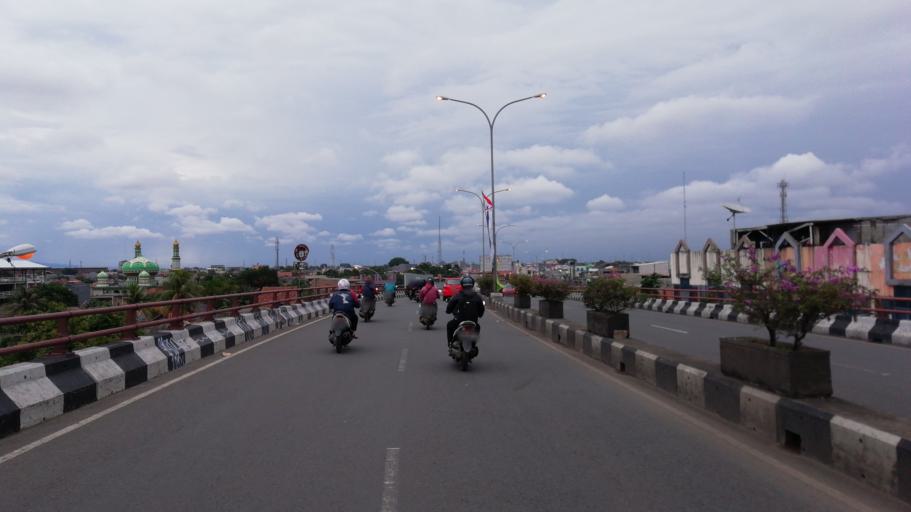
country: ID
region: West Java
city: Depok
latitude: -6.3901
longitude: 106.8219
